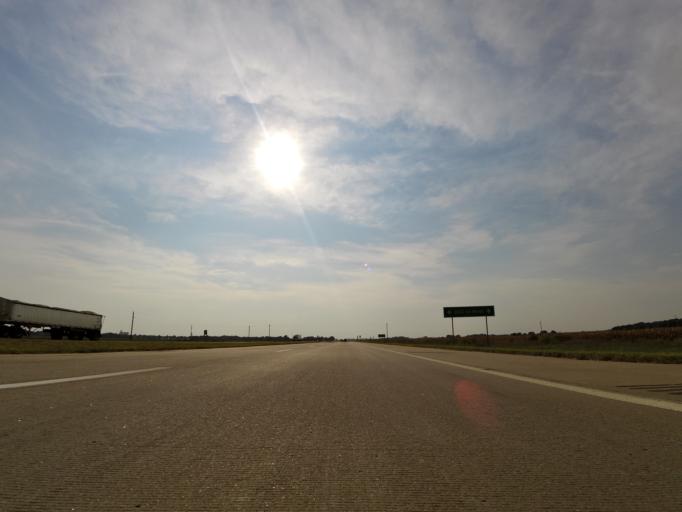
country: US
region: Kansas
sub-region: Reno County
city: Haven
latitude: 37.8762
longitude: -97.6447
